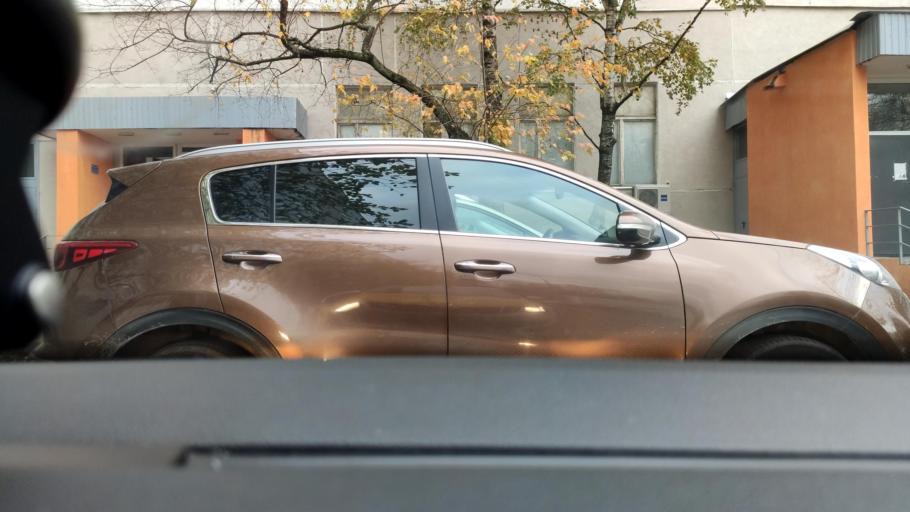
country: RU
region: Moscow
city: Lianozovo
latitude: 55.9033
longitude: 37.5721
